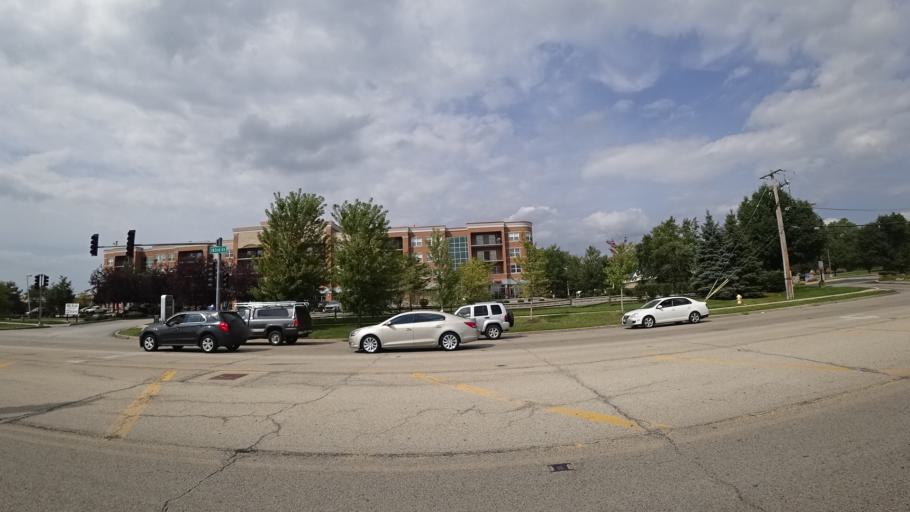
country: US
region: Illinois
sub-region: Cook County
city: Tinley Park
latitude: 41.5585
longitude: -87.7894
